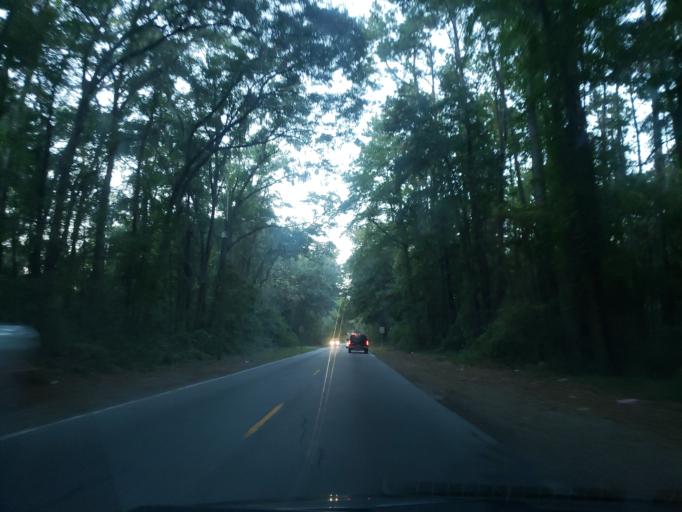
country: US
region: Georgia
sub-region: Chatham County
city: Isle of Hope
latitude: 32.0068
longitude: -81.0778
